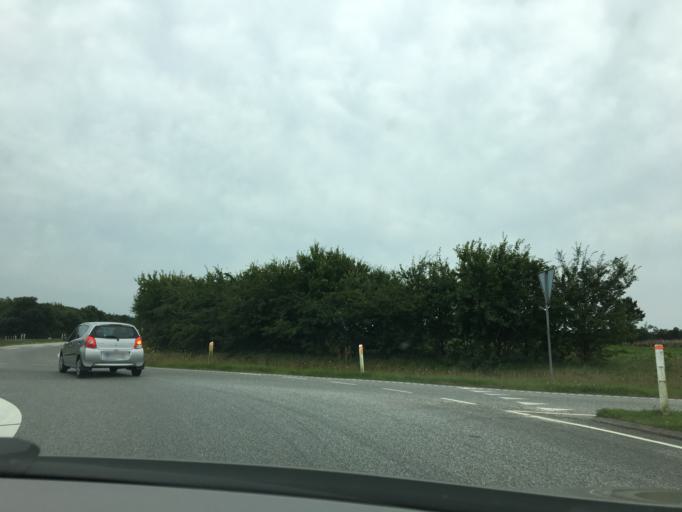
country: DK
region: Central Jutland
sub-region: Herning Kommune
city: Sunds
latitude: 56.2664
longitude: 9.0037
